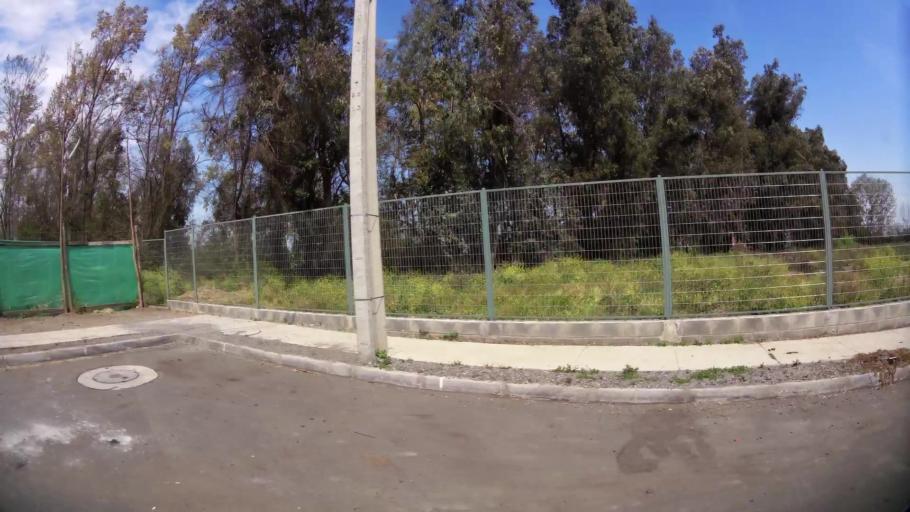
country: CL
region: Santiago Metropolitan
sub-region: Provincia de Talagante
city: Talagante
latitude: -33.6704
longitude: -70.9219
